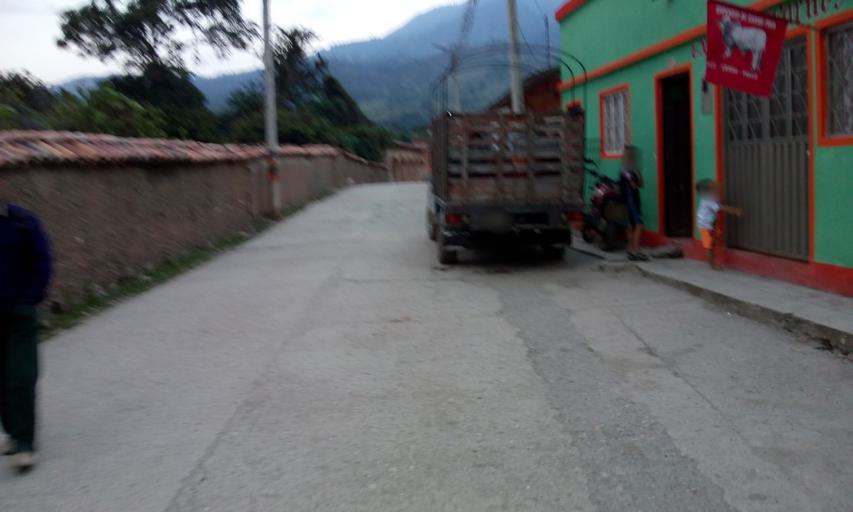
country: CO
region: Boyaca
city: Tipacoque
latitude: 6.4214
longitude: -72.6929
